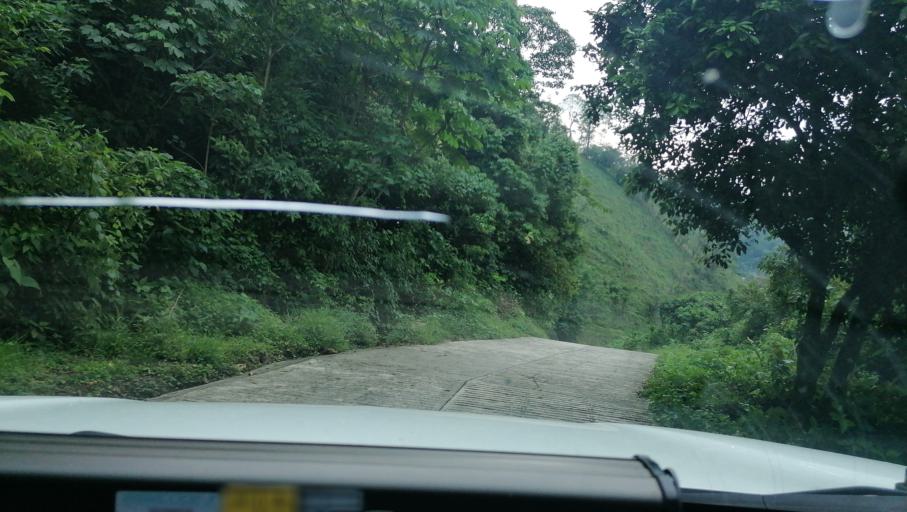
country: MX
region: Chiapas
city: Ixtacomitan
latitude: 17.3406
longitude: -93.1219
